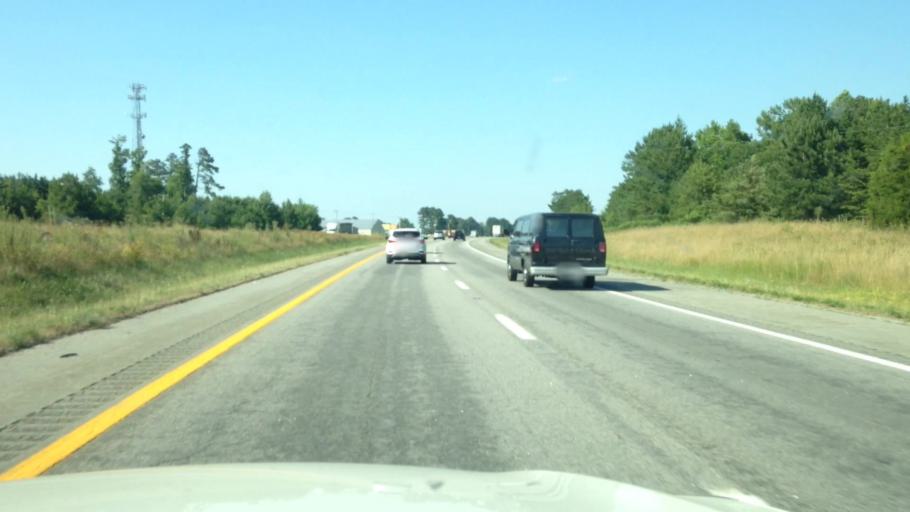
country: US
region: Virginia
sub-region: City of Emporia
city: Emporia
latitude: 36.8260
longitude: -77.4532
